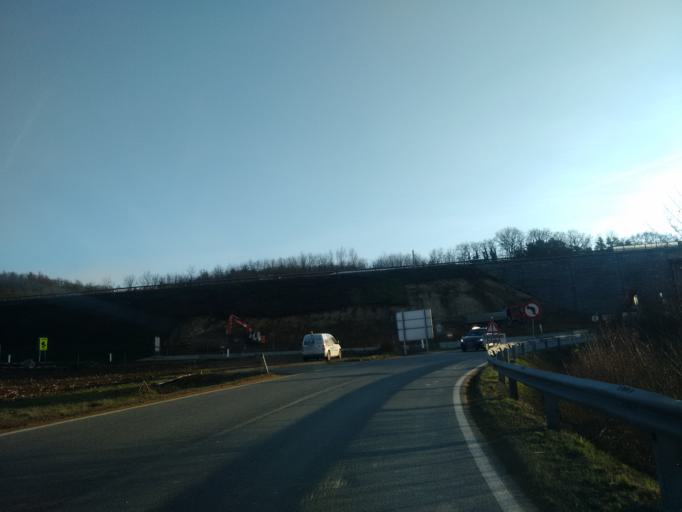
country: AT
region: Lower Austria
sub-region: Politischer Bezirk Melk
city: Klein-Poechlarn
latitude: 48.1973
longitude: 15.2219
